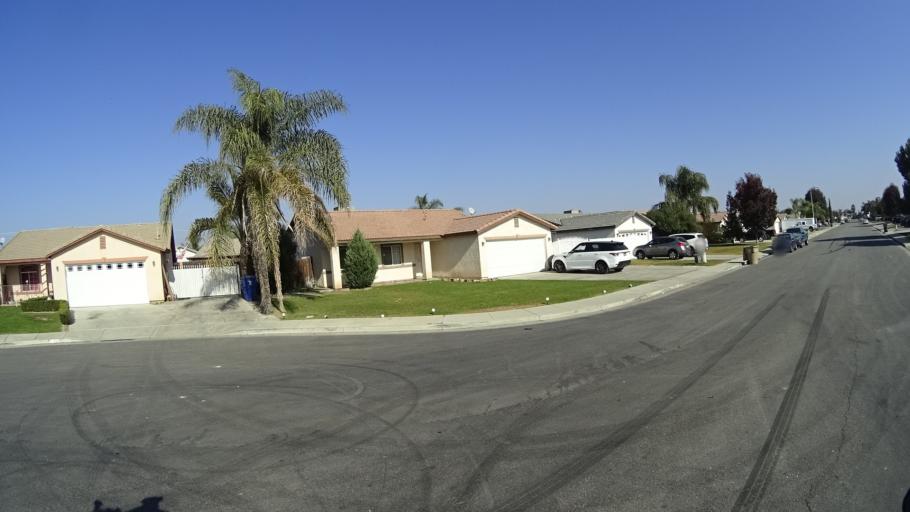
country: US
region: California
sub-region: Kern County
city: Greenfield
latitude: 35.2800
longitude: -119.0195
